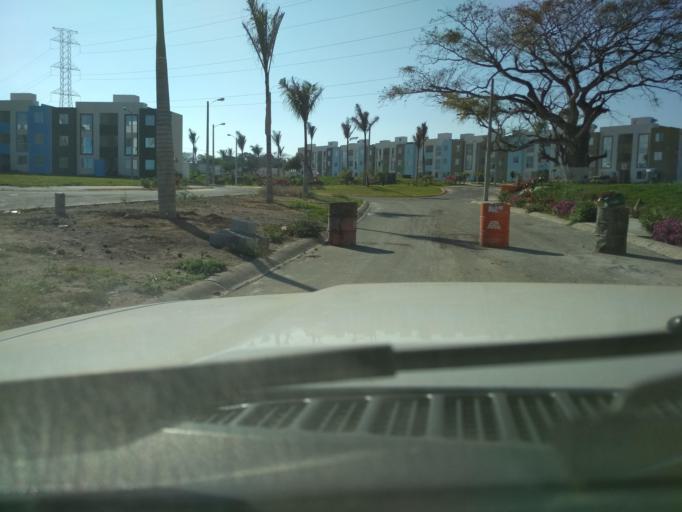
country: MX
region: Veracruz
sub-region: Veracruz
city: Las Amapolas
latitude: 19.1450
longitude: -96.2335
